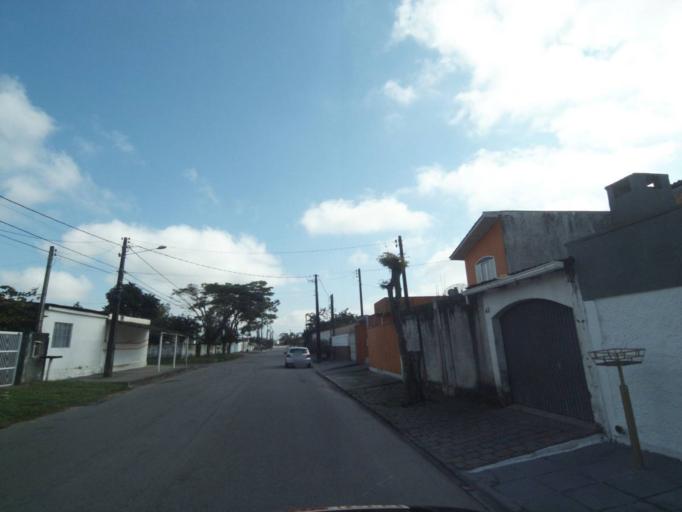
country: BR
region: Parana
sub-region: Paranagua
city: Paranagua
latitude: -25.5486
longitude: -48.5407
